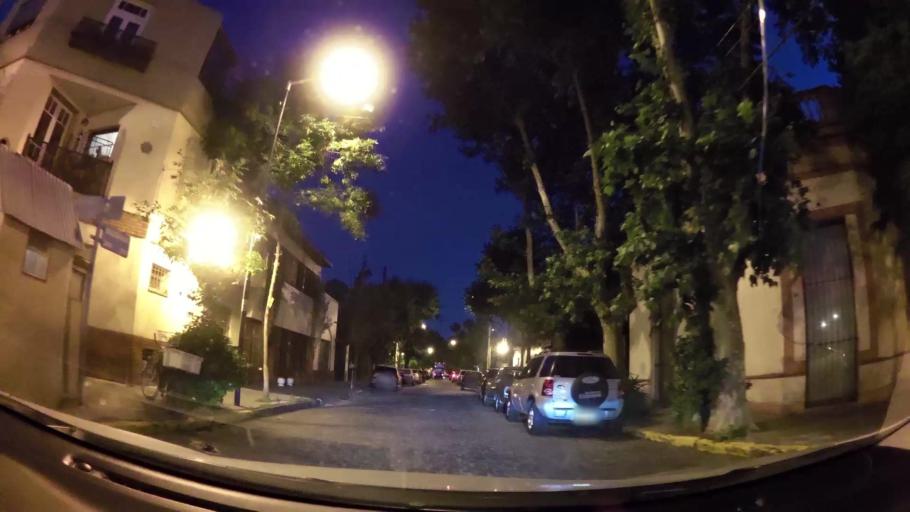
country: AR
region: Buenos Aires
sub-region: Partido de Tigre
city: Tigre
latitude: -34.4524
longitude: -58.5468
